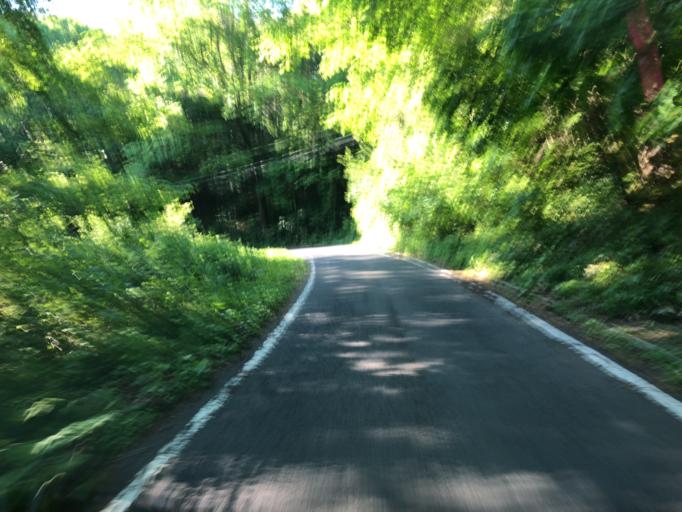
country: JP
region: Ibaraki
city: Kitaibaraki
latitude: 36.9071
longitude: 140.5877
